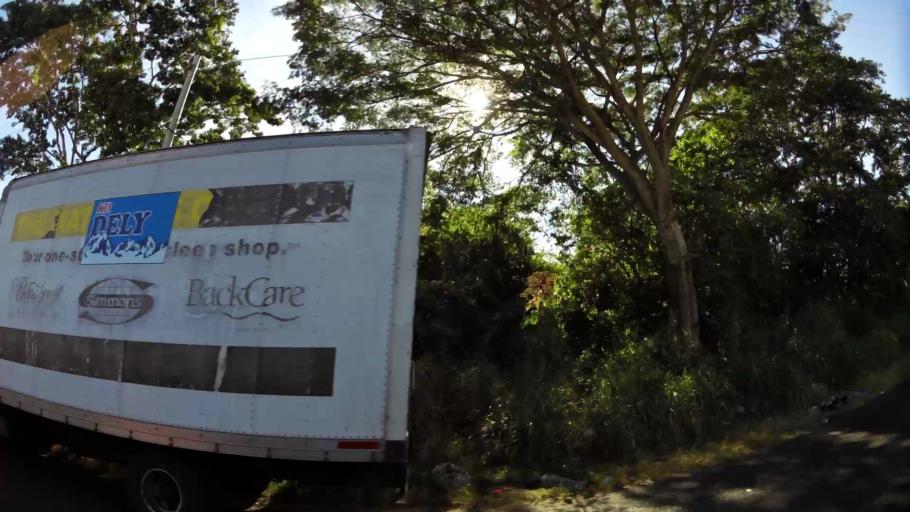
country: SV
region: Santa Ana
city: Santa Ana
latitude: 13.9605
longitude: -89.5769
